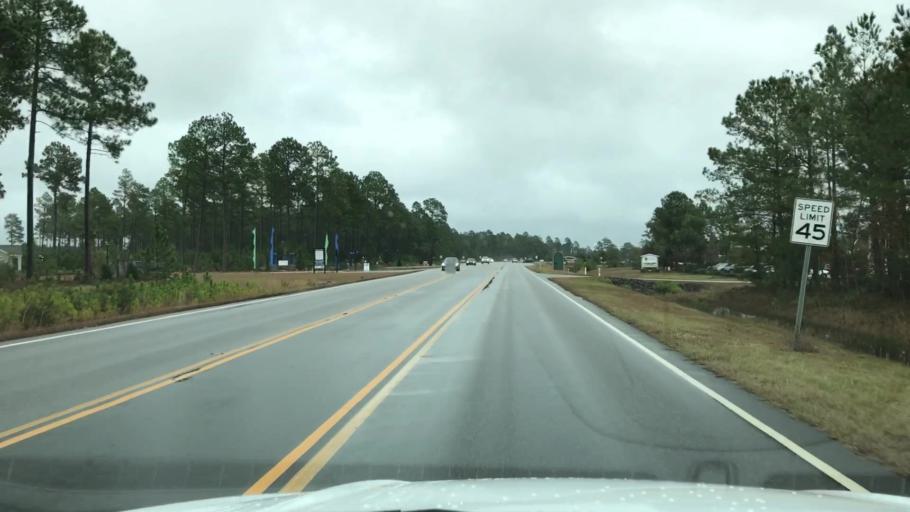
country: US
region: South Carolina
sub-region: Horry County
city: Myrtle Beach
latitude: 33.7604
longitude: -78.8943
